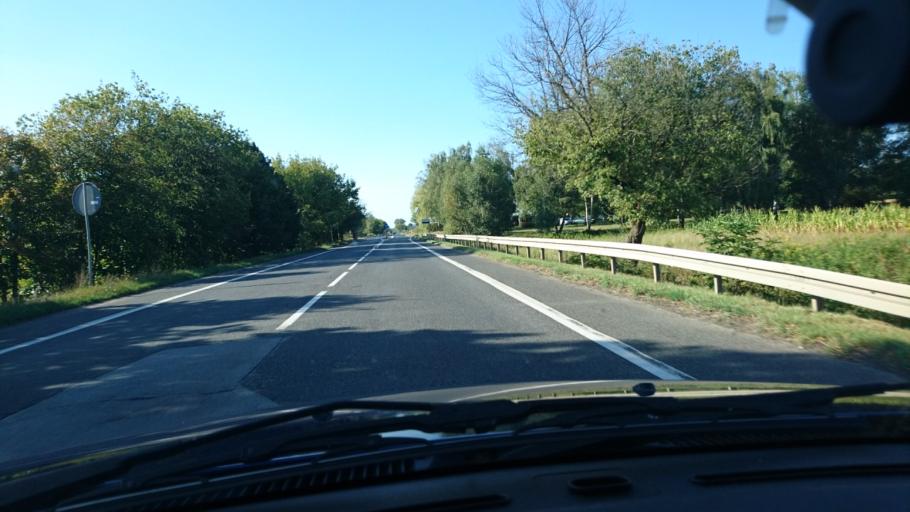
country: PL
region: Silesian Voivodeship
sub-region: Powiat gliwicki
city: Pyskowice
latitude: 50.3579
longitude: 18.6429
